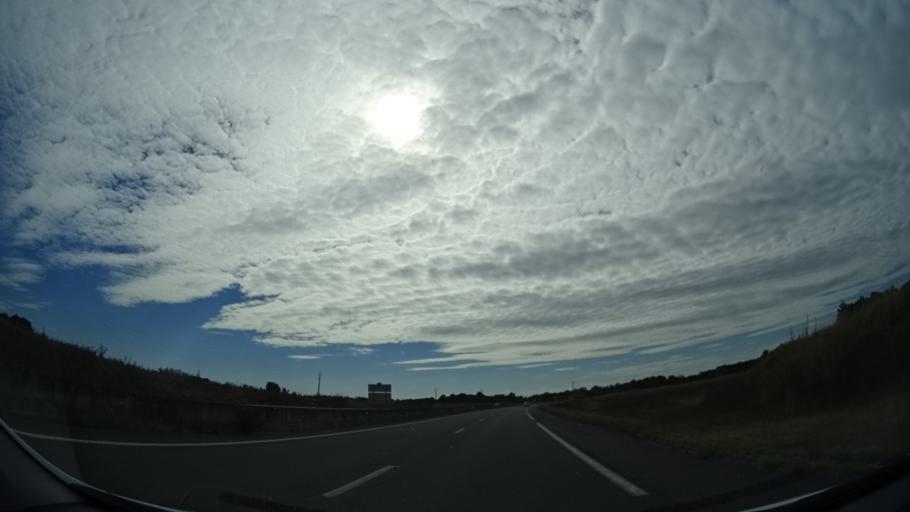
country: FR
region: Centre
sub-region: Departement du Loiret
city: Saint-Maurice-sur-Fessard
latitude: 47.9874
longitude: 2.6490
